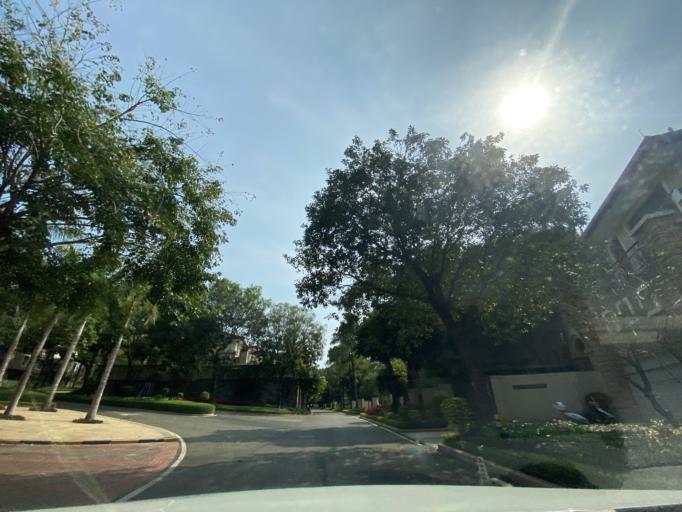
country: CN
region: Hainan
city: Yingzhou
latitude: 18.4111
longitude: 109.8435
